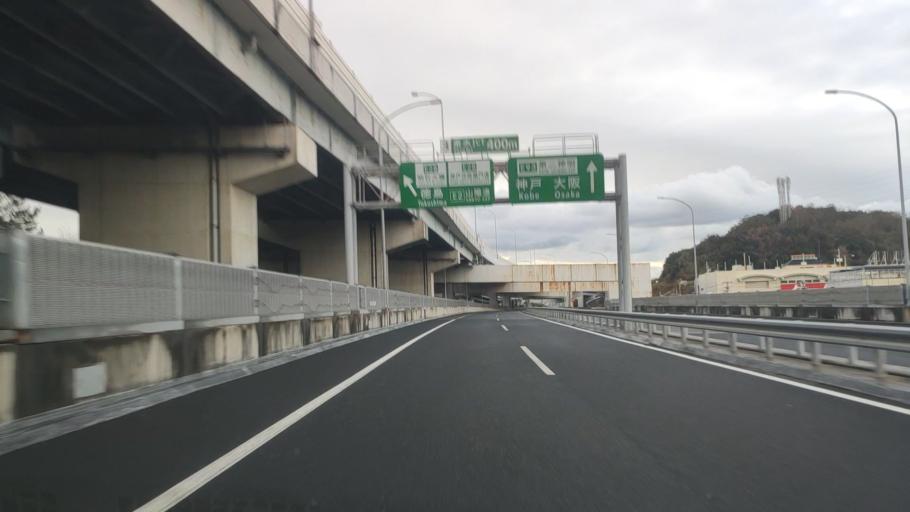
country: JP
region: Hyogo
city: Akashi
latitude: 34.6661
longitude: 135.0675
